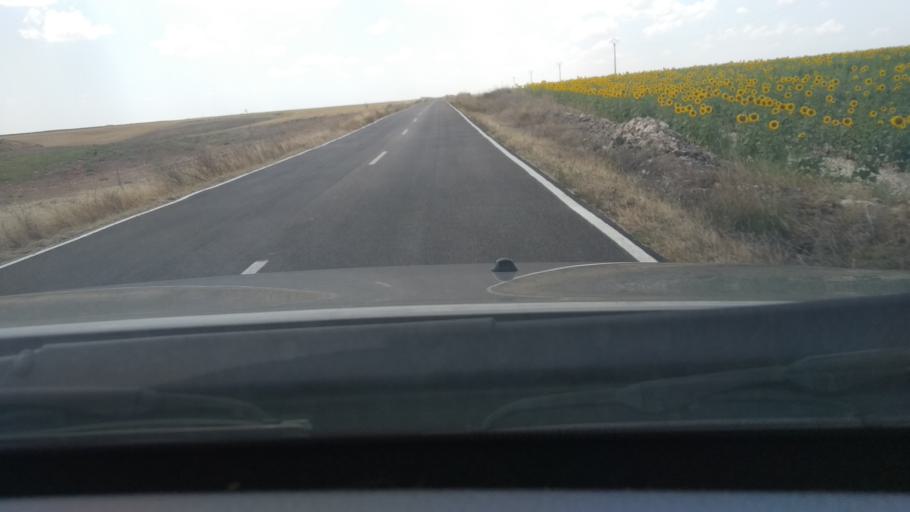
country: ES
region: Castille and Leon
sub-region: Provincia de Burgos
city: Iglesiarrubia
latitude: 41.9404
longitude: -3.8703
